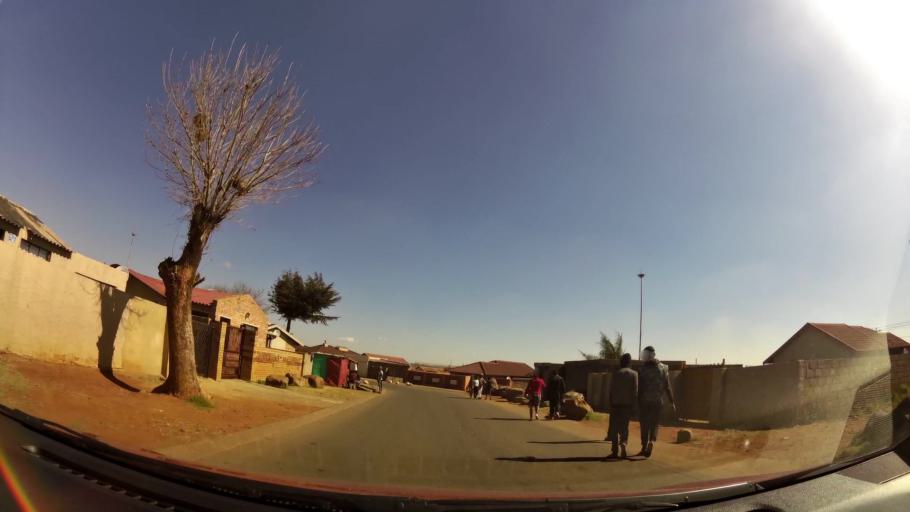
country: ZA
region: Gauteng
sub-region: City of Johannesburg Metropolitan Municipality
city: Soweto
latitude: -26.2375
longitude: 27.8224
